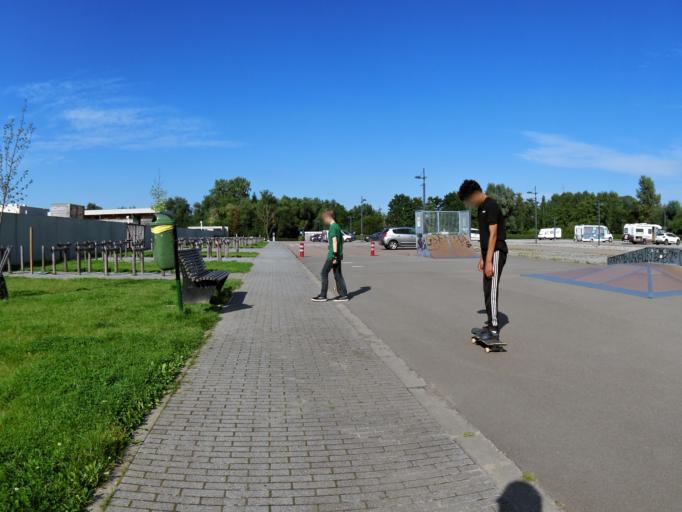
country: BE
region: Flanders
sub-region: Provincie Limburg
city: Tongeren
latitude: 50.7850
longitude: 5.4514
